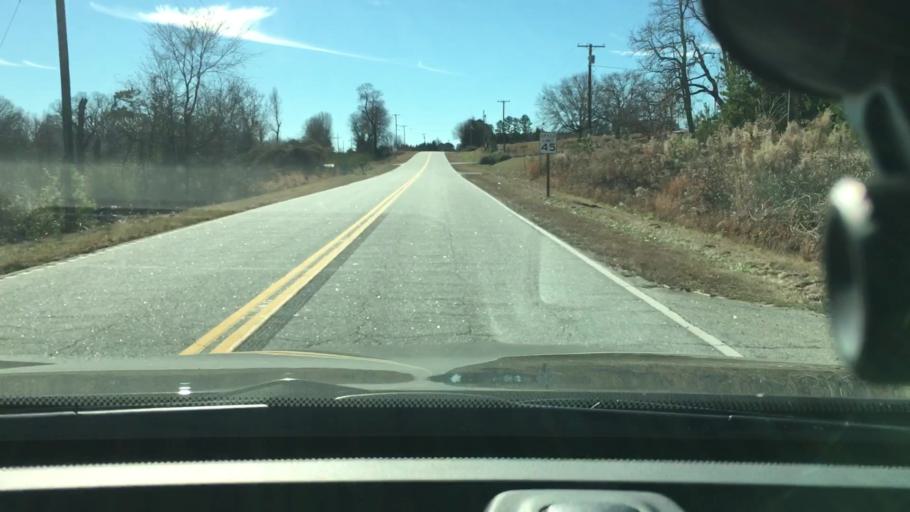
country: US
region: South Carolina
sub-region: Spartanburg County
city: Pacolet
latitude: 34.9463
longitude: -81.7180
